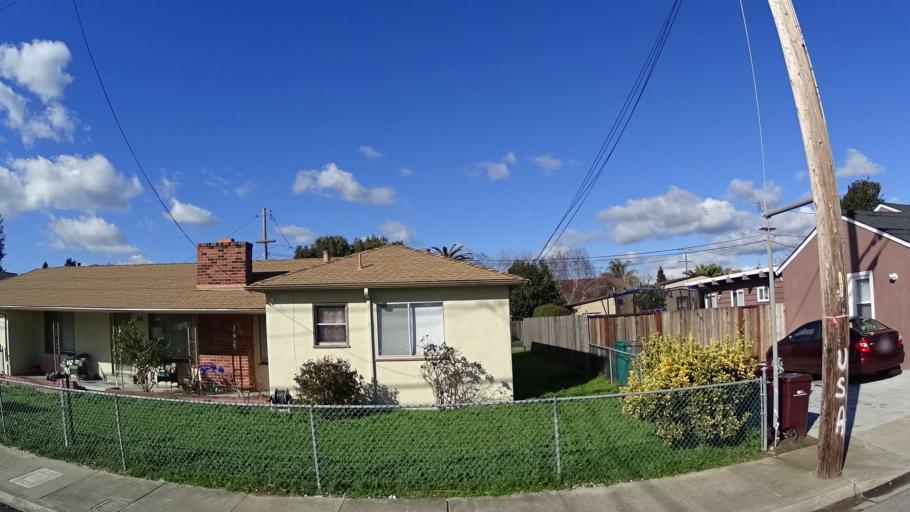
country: US
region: California
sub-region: Alameda County
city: Cherryland
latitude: 37.6804
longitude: -122.1103
